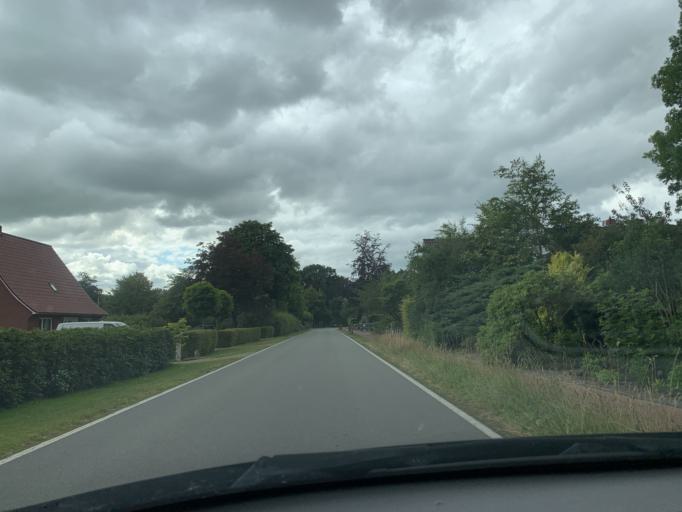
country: DE
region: Lower Saxony
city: Westerstede
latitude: 53.2337
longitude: 7.8784
